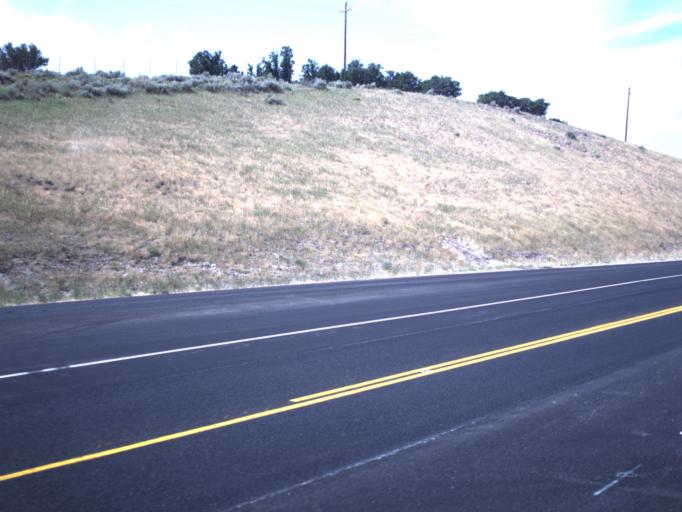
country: US
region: Utah
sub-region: Summit County
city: Kamas
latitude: 40.6342
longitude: -111.3464
